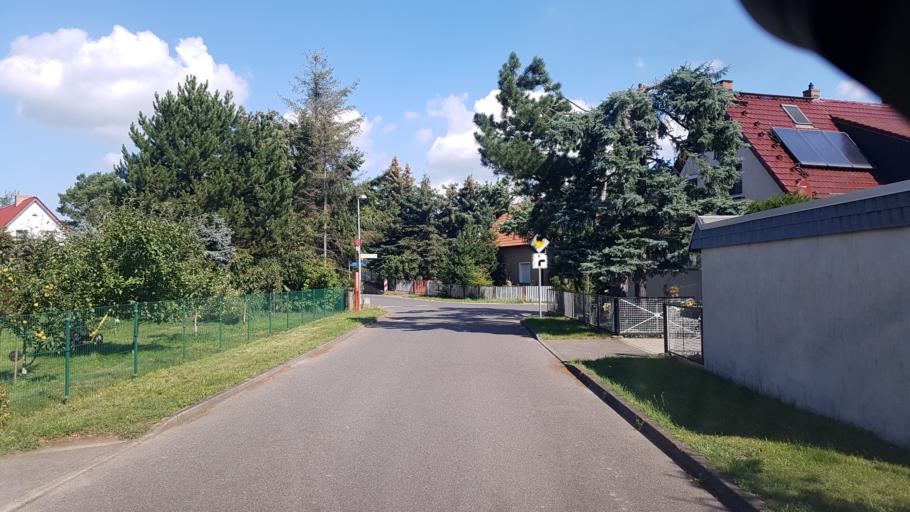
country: DE
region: Brandenburg
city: Drebkau
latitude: 51.6717
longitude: 14.2290
